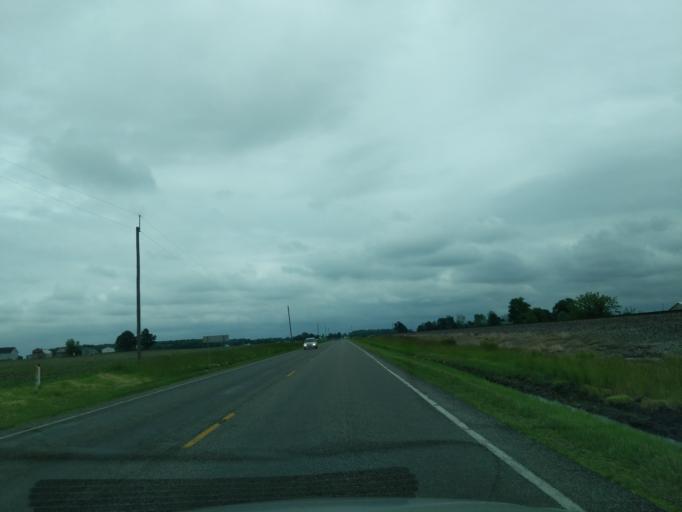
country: US
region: Indiana
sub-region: Madison County
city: Elwood
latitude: 40.2788
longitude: -85.8992
